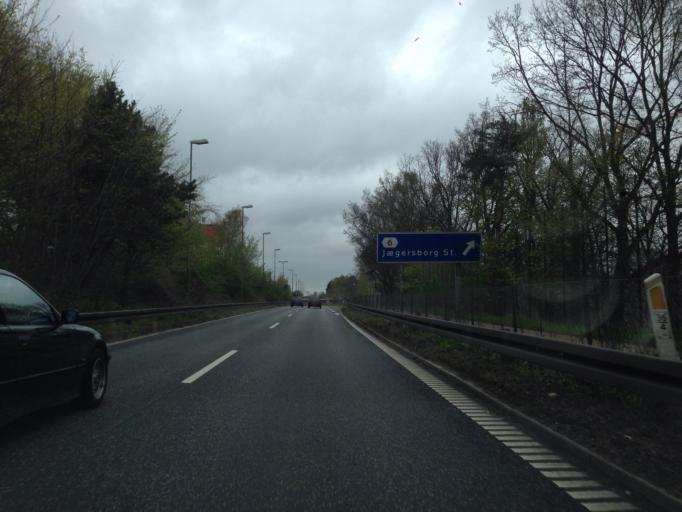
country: DK
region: Capital Region
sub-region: Lyngby-Tarbaek Kommune
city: Kongens Lyngby
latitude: 55.7579
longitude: 12.5218
